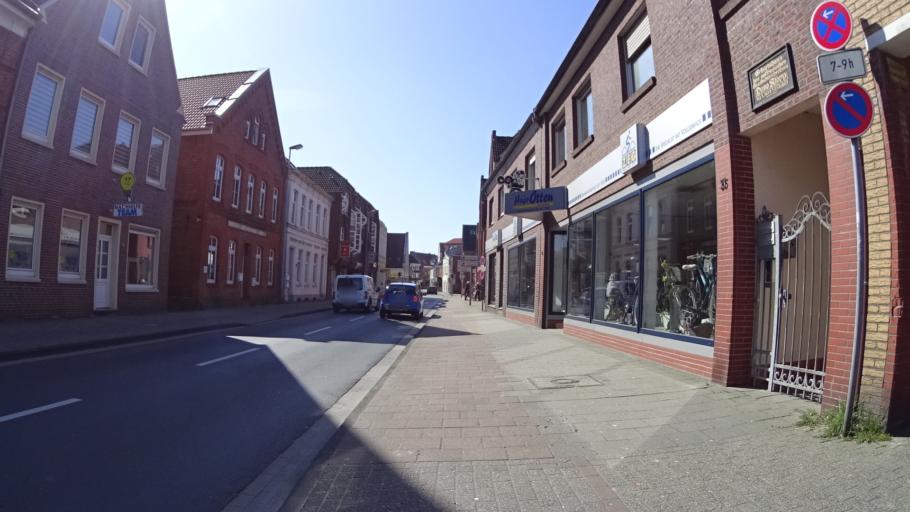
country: DE
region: Lower Saxony
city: Leer
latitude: 53.2311
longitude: 7.4515
